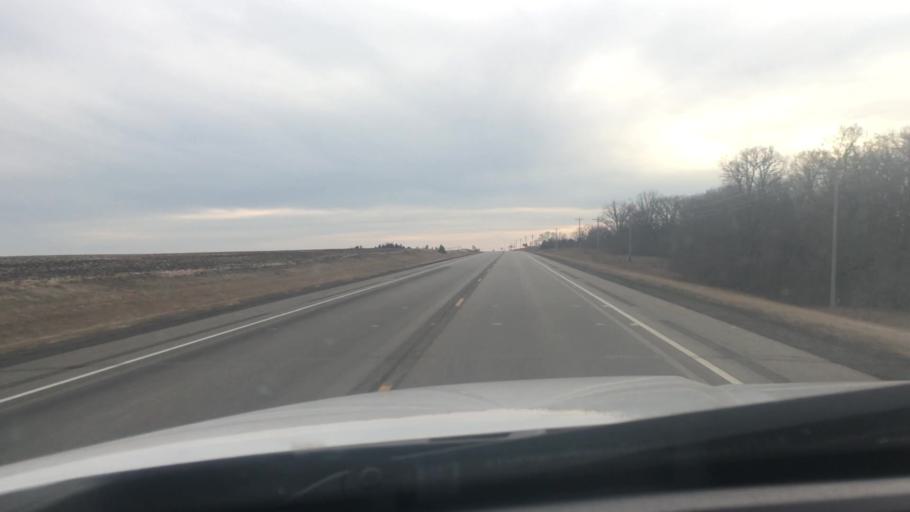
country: US
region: Minnesota
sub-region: Otter Tail County
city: Perham
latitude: 46.3165
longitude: -95.7185
